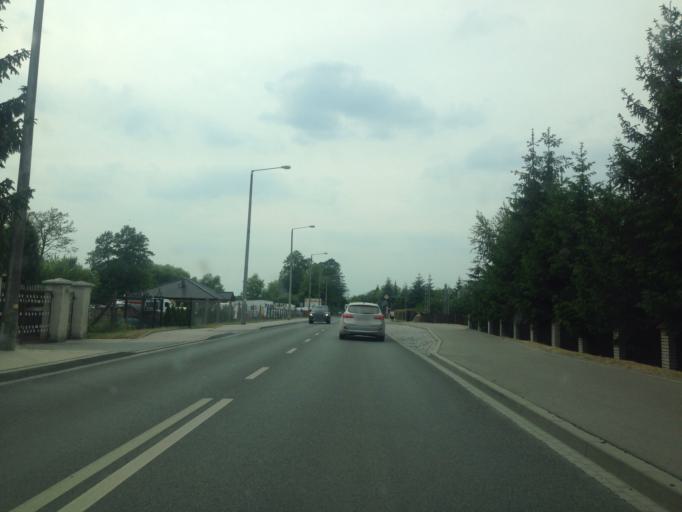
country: PL
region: Kujawsko-Pomorskie
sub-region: Powiat grudziadzki
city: Rogozno
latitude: 53.5020
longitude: 18.8506
